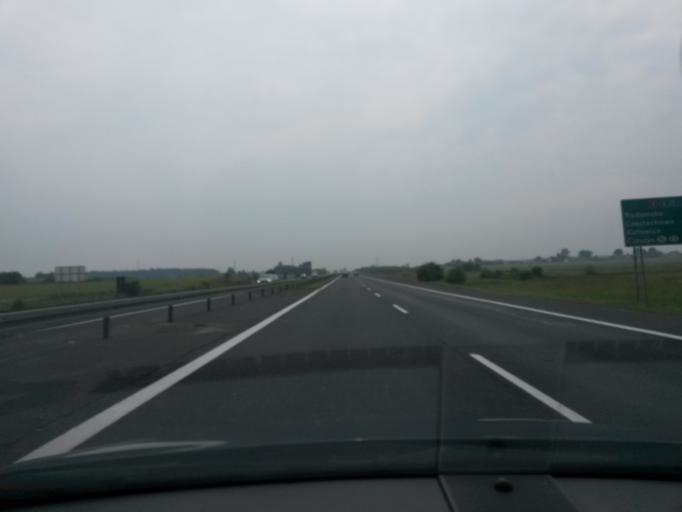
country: PL
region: Lodz Voivodeship
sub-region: Piotrkow Trybunalski
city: Piotrkow Trybunalski
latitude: 51.4042
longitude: 19.6328
